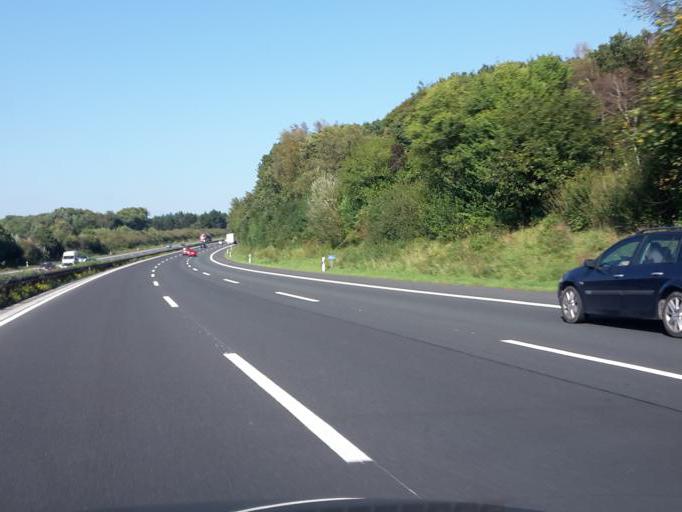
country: DE
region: North Rhine-Westphalia
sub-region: Regierungsbezirk Koln
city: Stossdorf
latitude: 50.7574
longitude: 7.2295
